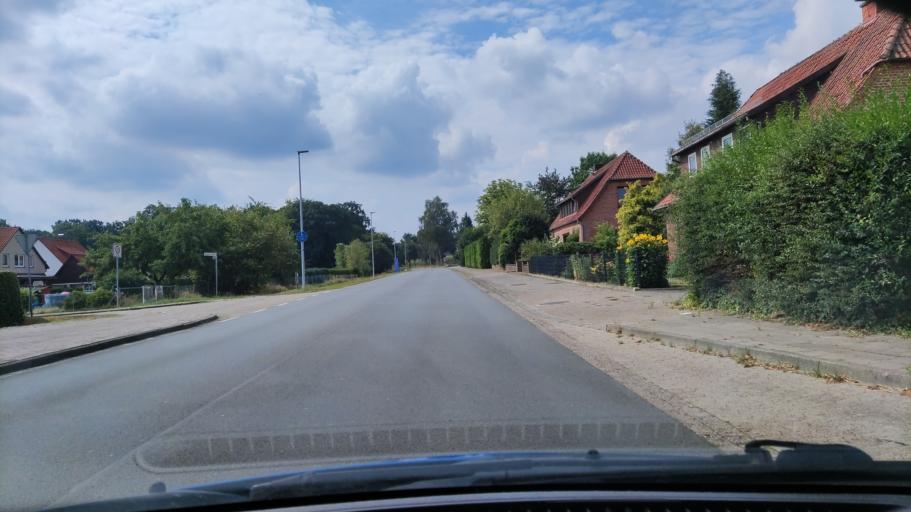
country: DE
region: Lower Saxony
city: Bad Fallingbostel
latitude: 52.8966
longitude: 9.7553
